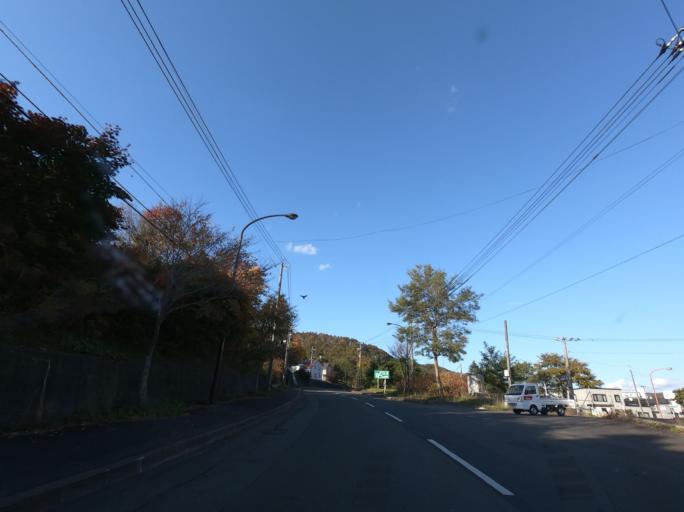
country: JP
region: Hokkaido
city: Iwamizawa
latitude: 43.0442
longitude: 141.9629
